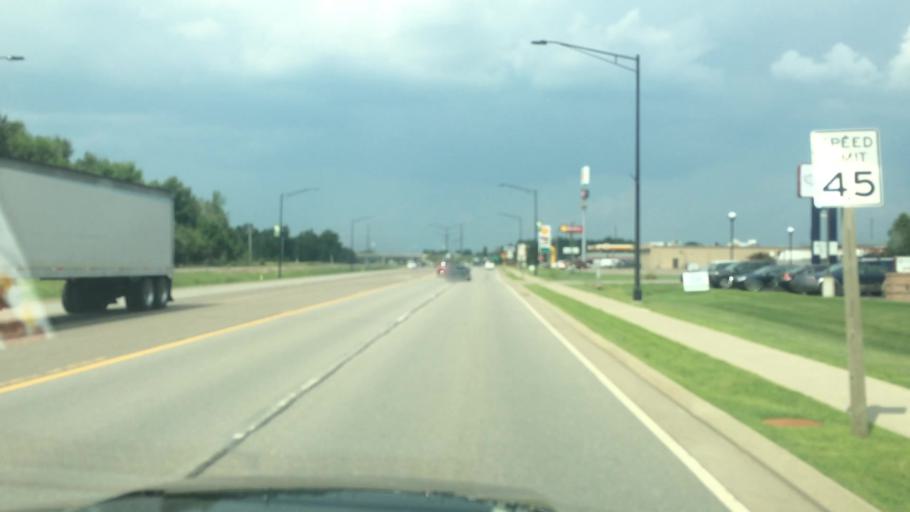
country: US
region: Wisconsin
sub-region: Clark County
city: Colby
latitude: 44.9267
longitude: -90.3154
